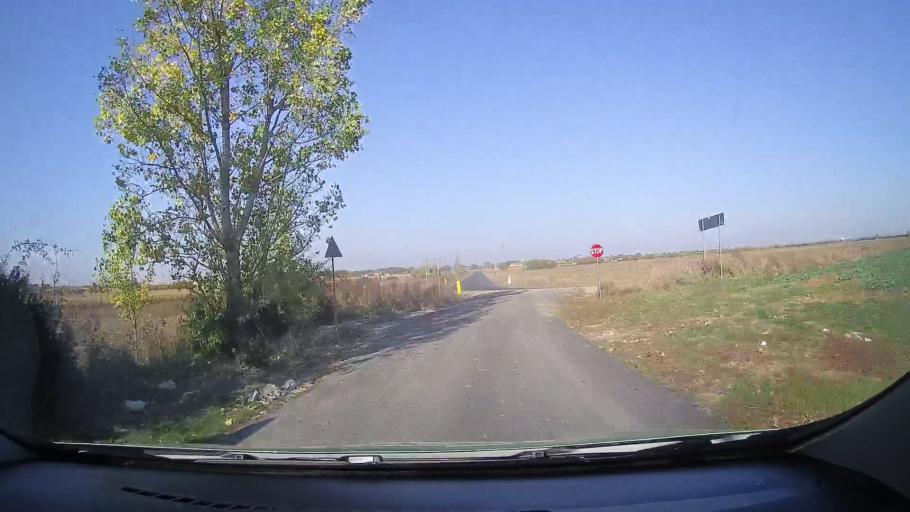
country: RO
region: Satu Mare
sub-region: Comuna Sauca
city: Sauca
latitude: 47.4857
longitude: 22.4625
